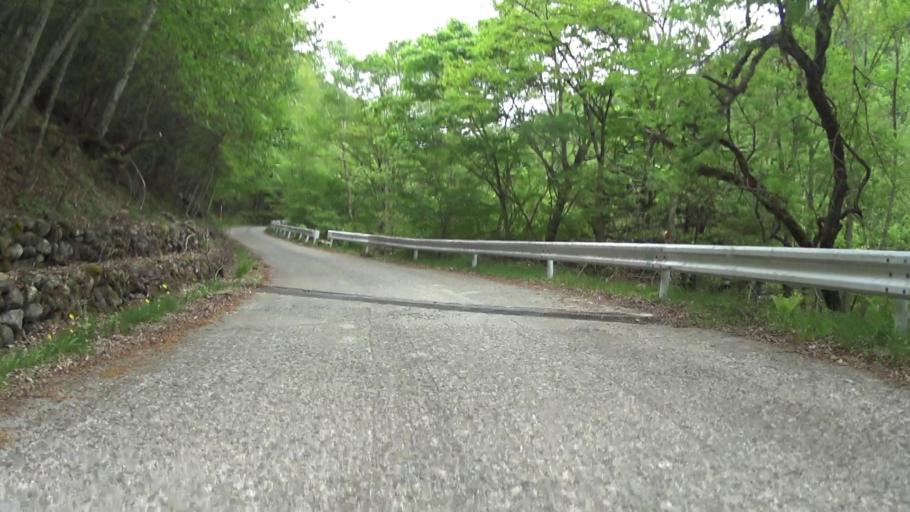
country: JP
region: Yamanashi
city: Kofu-shi
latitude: 35.8457
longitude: 138.5772
